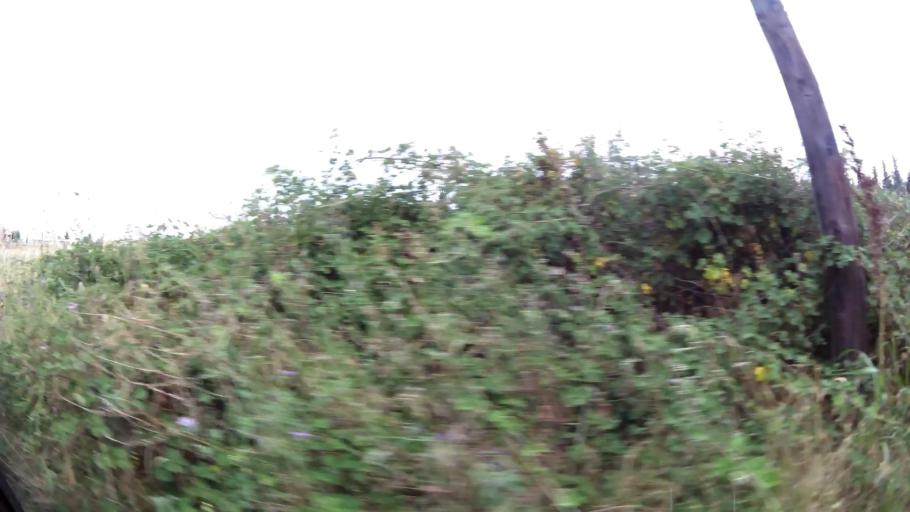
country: GR
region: Central Macedonia
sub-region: Nomos Thessalonikis
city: Oraiokastro
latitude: 40.7065
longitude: 22.9290
